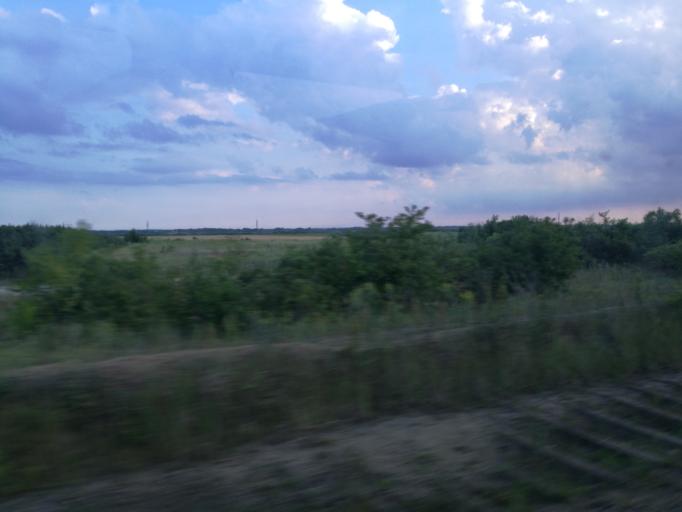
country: RO
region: Dambovita
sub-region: Comuna Produlesti
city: Costestii din Deal
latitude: 44.6746
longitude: 25.4987
